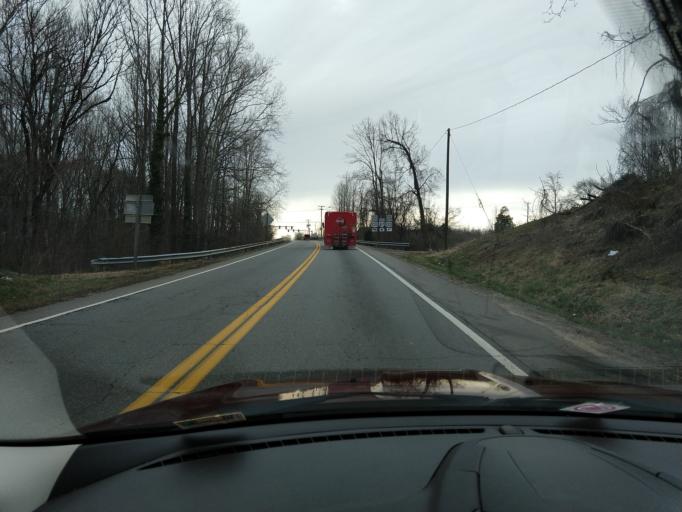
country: US
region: Virginia
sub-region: Henry County
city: Chatmoss
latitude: 36.5777
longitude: -79.8610
